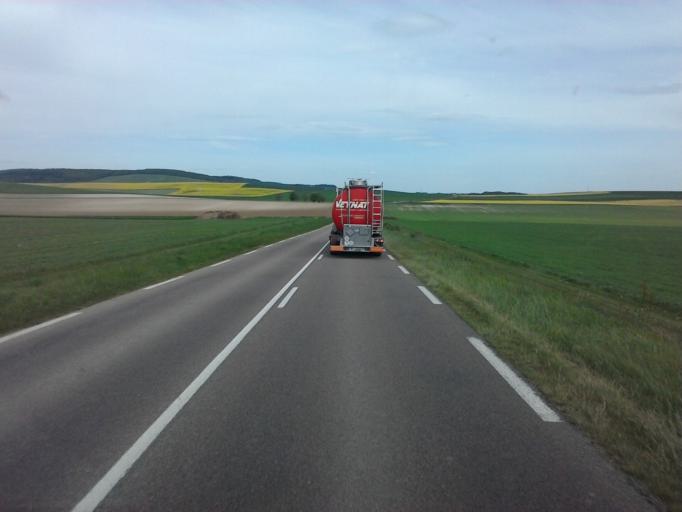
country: FR
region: Champagne-Ardenne
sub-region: Departement de l'Aube
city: Ervy-le-Chatel
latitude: 48.0997
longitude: 3.8698
